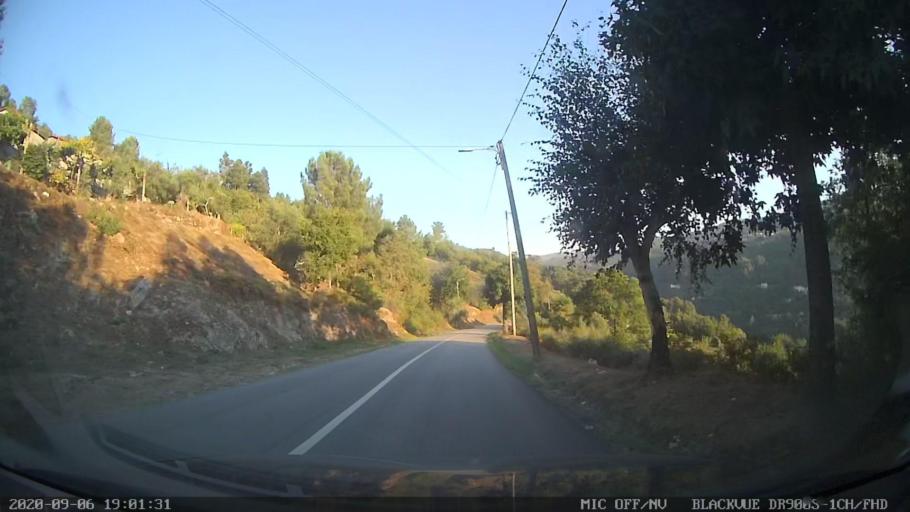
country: PT
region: Porto
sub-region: Baiao
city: Baiao
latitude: 41.2339
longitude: -7.9980
